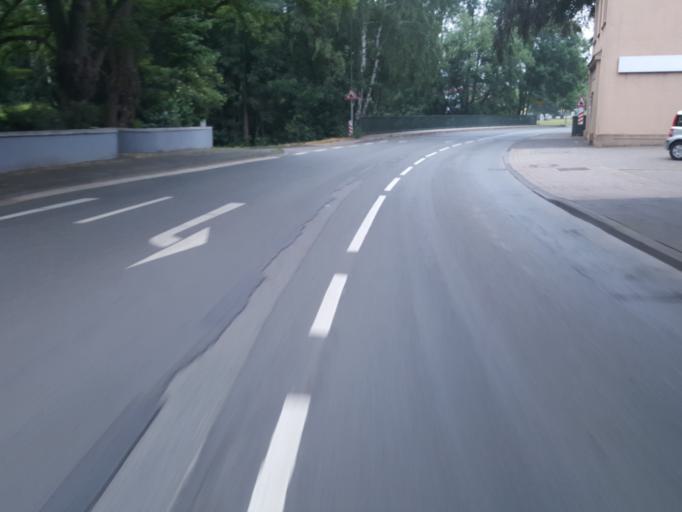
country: DE
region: North Rhine-Westphalia
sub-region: Regierungsbezirk Detmold
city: Kirchlengern
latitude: 52.1946
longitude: 8.6408
